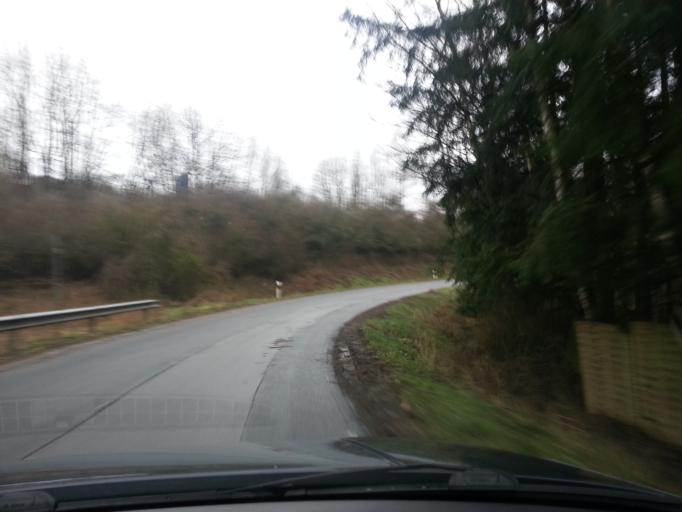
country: DE
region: Rheinland-Pfalz
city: Konken
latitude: 49.5131
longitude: 7.3578
